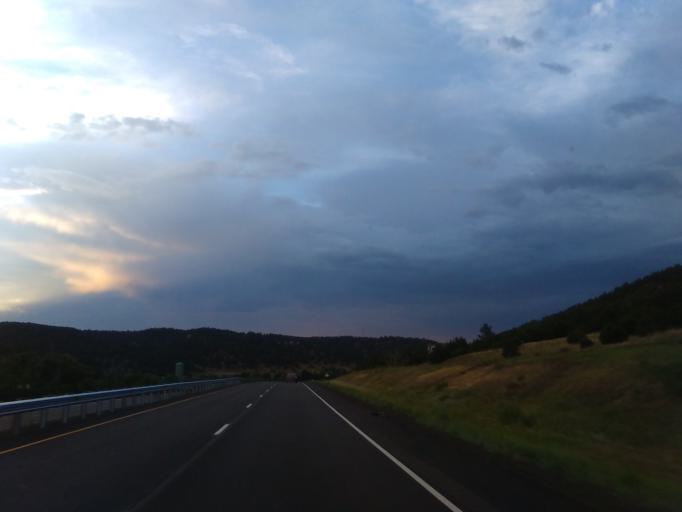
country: US
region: Colorado
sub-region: Las Animas County
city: Trinidad
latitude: 37.1004
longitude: -104.5221
